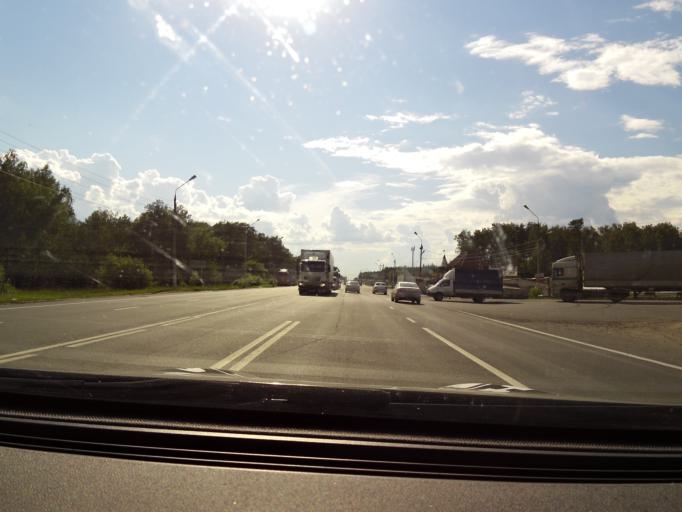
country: RU
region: Nizjnij Novgorod
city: Gorbatovka
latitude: 56.3090
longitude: 43.7475
